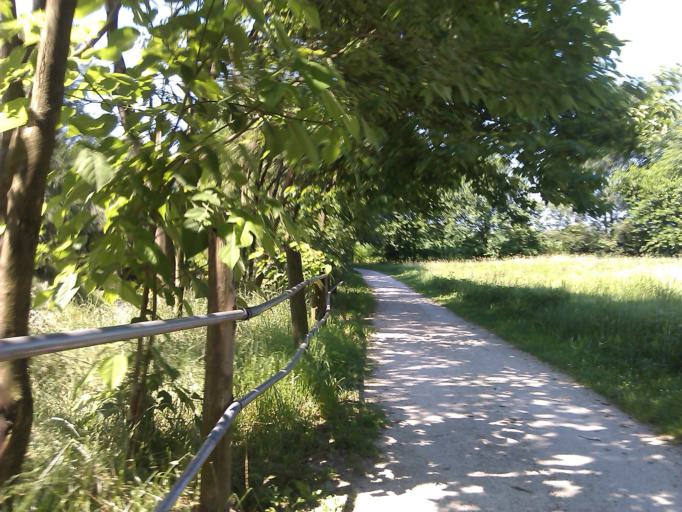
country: IT
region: Veneto
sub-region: Provincia di Treviso
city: Ramon
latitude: 45.7122
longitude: 11.8793
